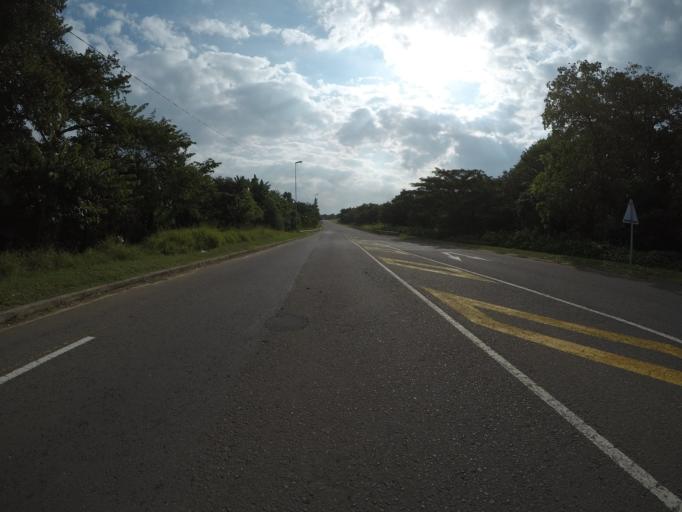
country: ZA
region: KwaZulu-Natal
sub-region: uThungulu District Municipality
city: Richards Bay
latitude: -28.7379
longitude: 32.0718
